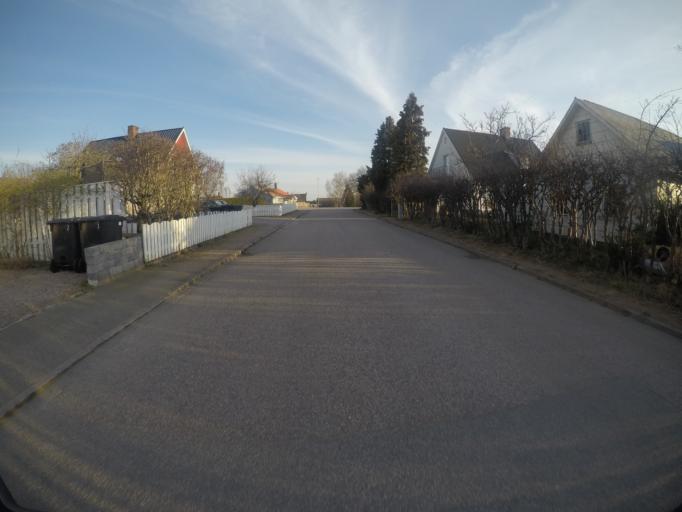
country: SE
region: Halland
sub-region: Laholms Kommun
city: Laholm
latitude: 56.5042
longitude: 13.0246
